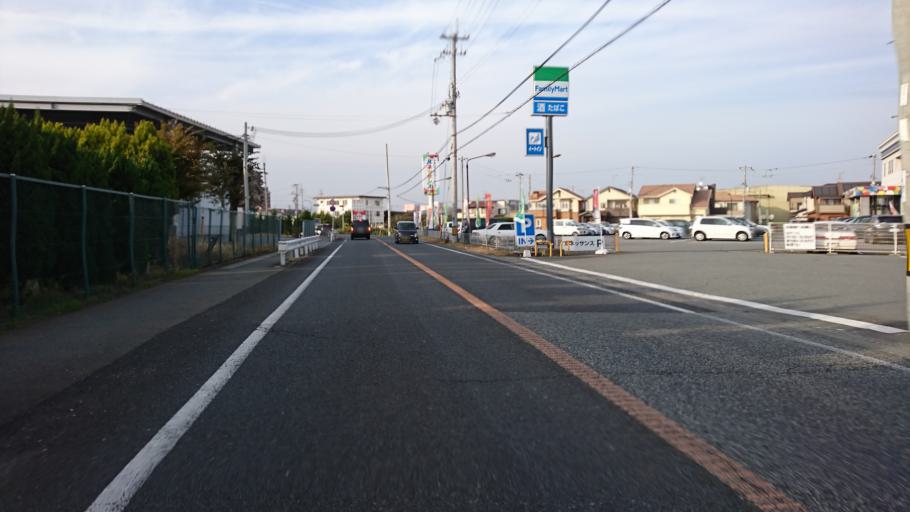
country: JP
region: Hyogo
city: Kakogawacho-honmachi
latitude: 34.7230
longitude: 134.8506
